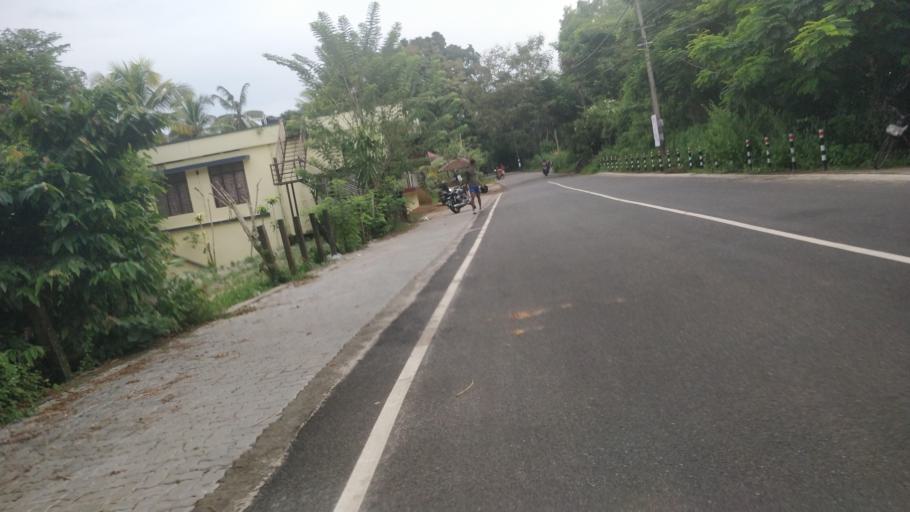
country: IN
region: Kerala
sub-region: Alappuzha
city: Shertallai
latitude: 9.6919
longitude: 76.3552
